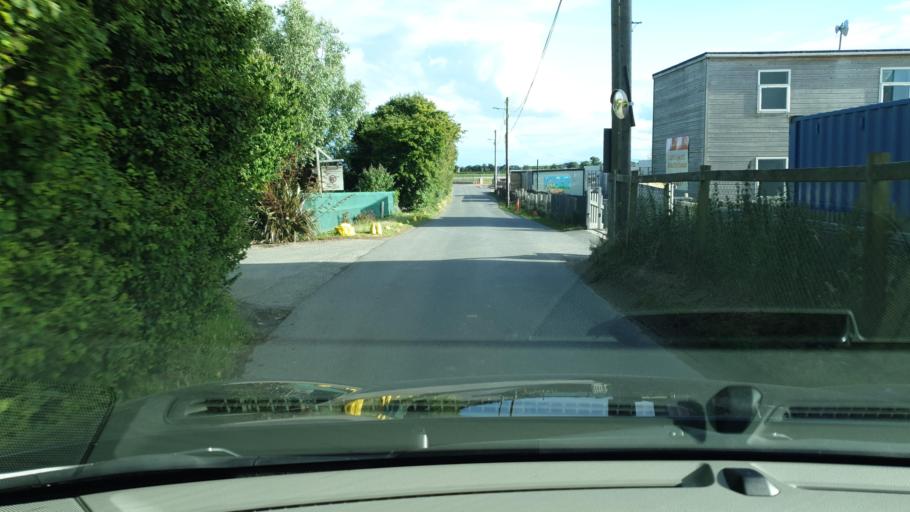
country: IE
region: Leinster
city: An Ros
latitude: 53.5330
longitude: -6.1053
